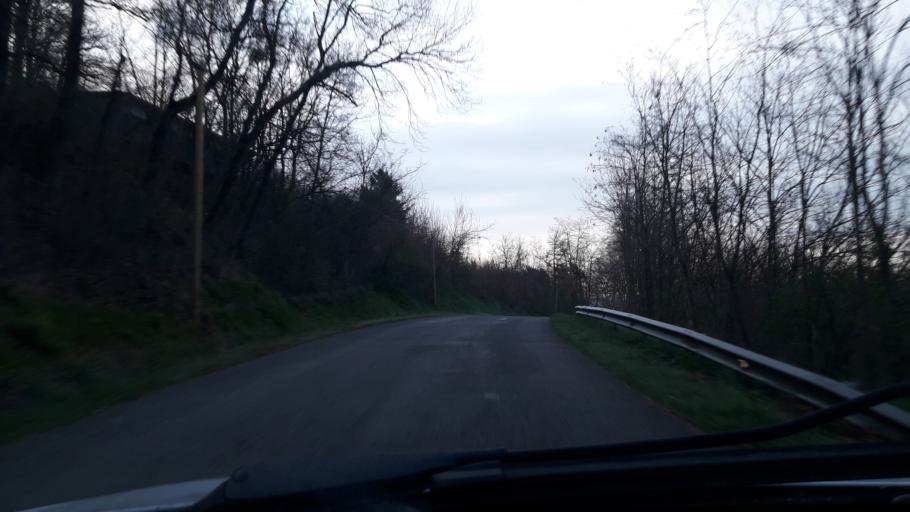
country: FR
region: Midi-Pyrenees
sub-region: Departement de la Haute-Garonne
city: Montesquieu-Volvestre
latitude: 43.2042
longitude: 1.2364
